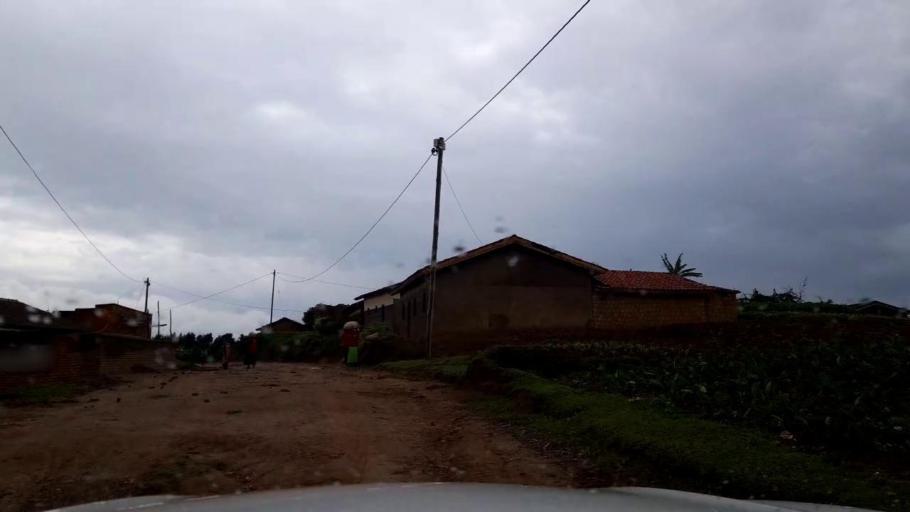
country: RW
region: Western Province
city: Kibuye
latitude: -2.0129
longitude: 29.4717
